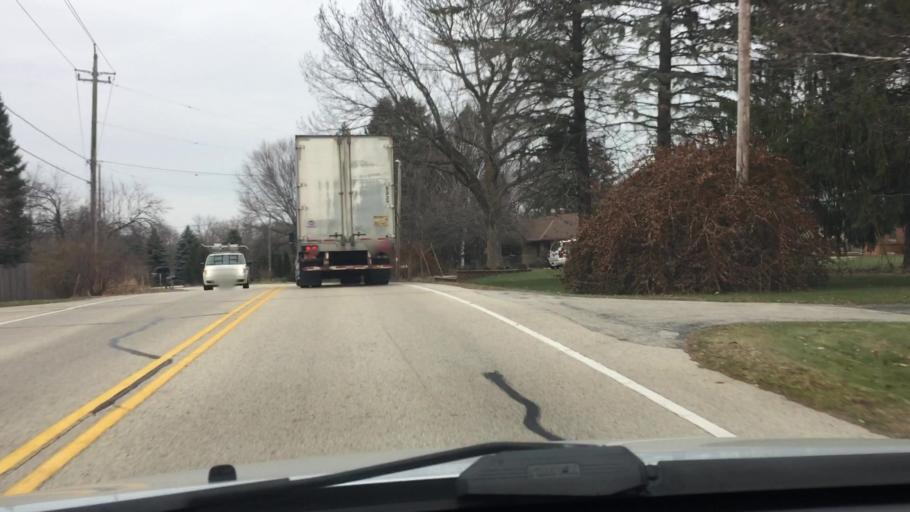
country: US
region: Wisconsin
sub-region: Ozaukee County
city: Grafton
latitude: 43.2961
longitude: -87.9599
